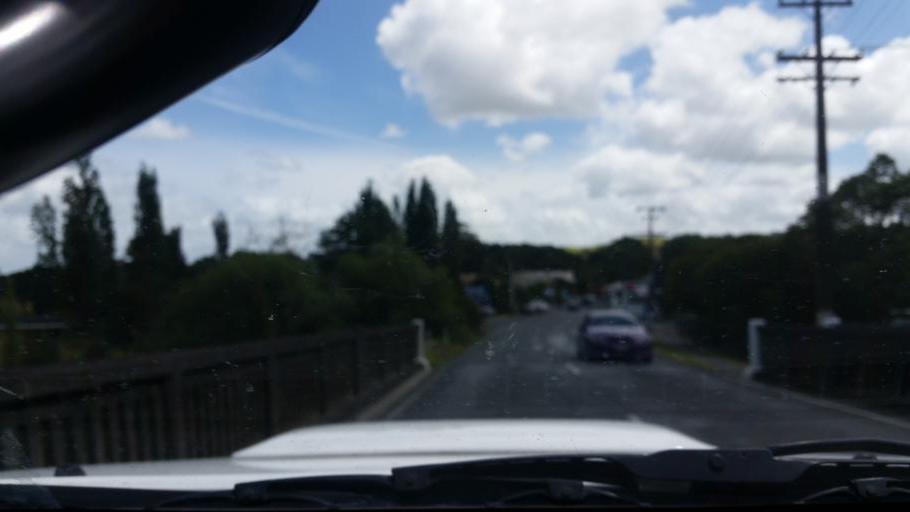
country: NZ
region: Northland
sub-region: Whangarei
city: Ruakaka
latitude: -36.0995
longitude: 174.2362
